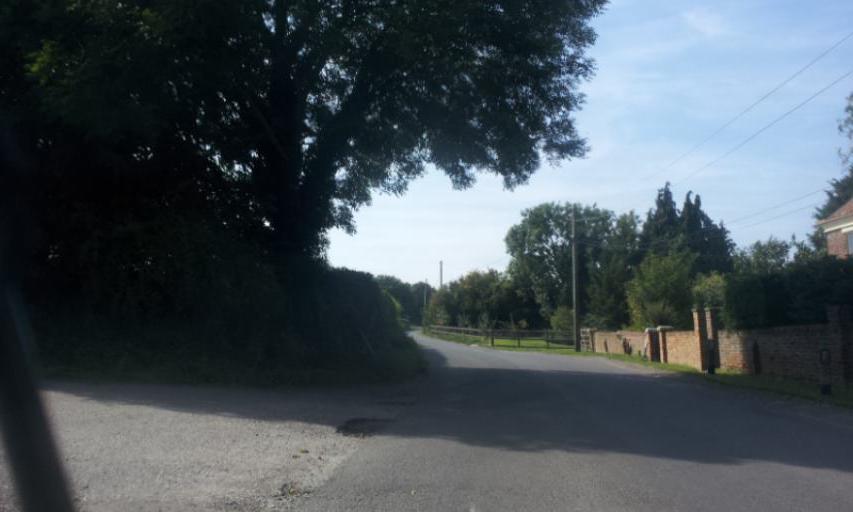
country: GB
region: England
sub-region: Kent
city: Newington
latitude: 51.3253
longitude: 0.6965
